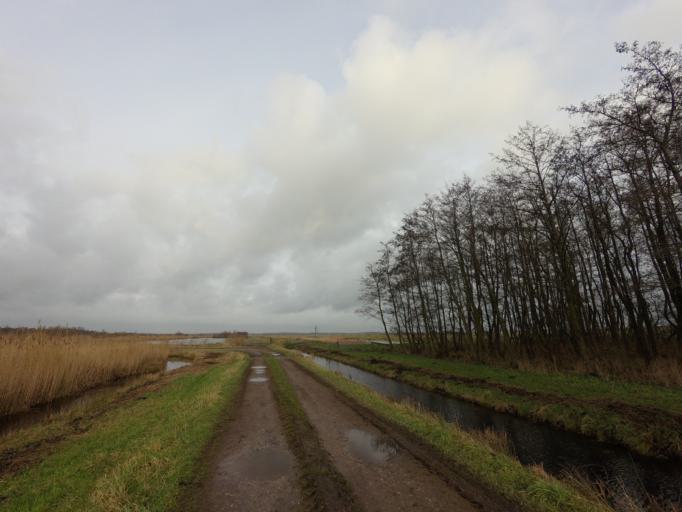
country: NL
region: North Holland
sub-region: Gemeente Wijdemeren
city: Nieuw-Loosdrecht
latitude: 52.1602
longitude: 5.1211
